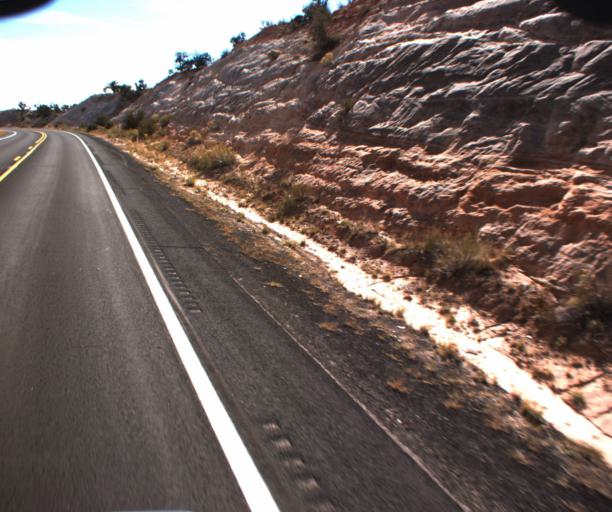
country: US
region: Arizona
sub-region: Coconino County
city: Kaibito
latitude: 36.5917
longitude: -110.8962
